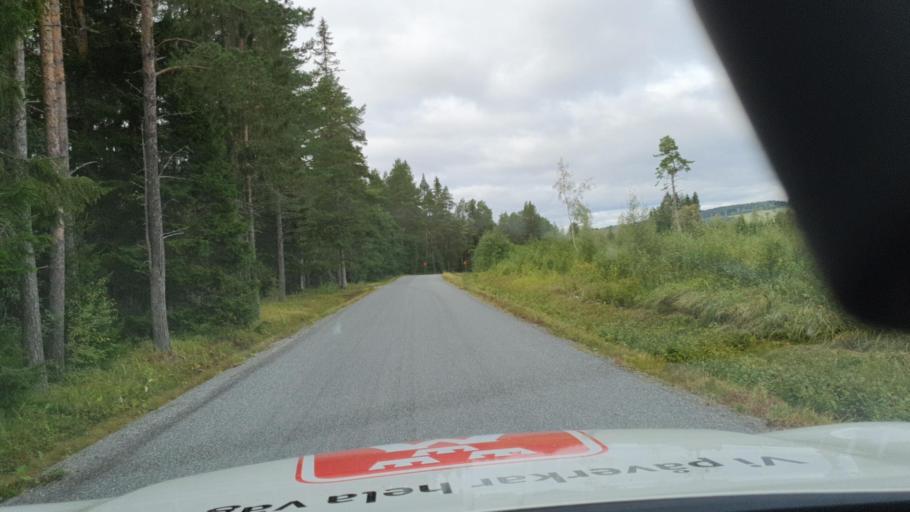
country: SE
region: Jaemtland
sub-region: OEstersunds Kommun
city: Ostersund
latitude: 63.1454
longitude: 14.5492
